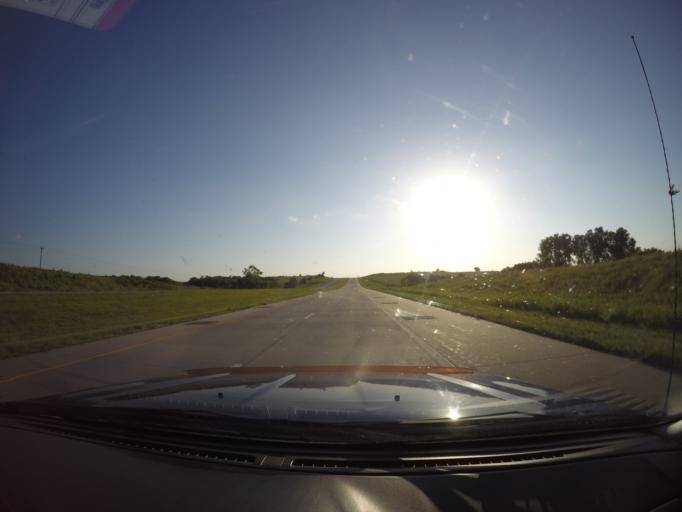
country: US
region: Kansas
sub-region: Pottawatomie County
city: Wamego
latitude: 39.2104
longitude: -96.3814
